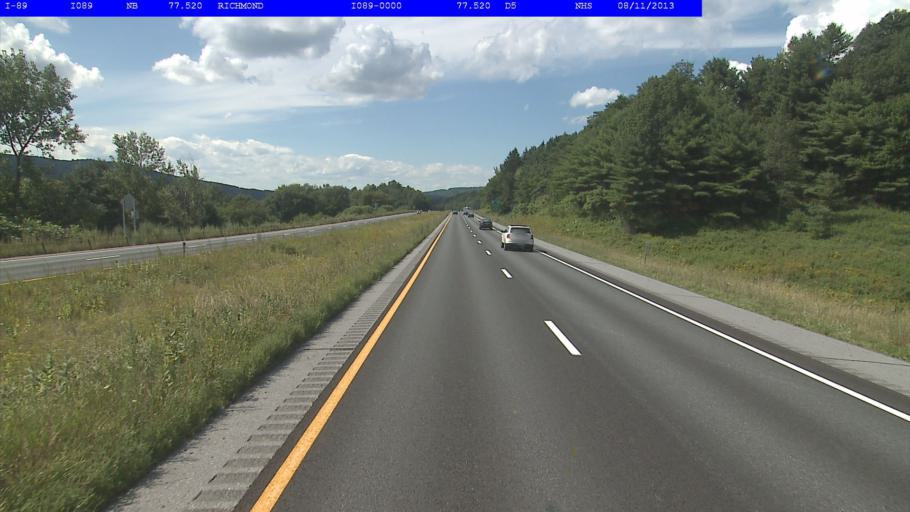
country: US
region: Vermont
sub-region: Chittenden County
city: Williston
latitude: 44.4170
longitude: -72.9964
